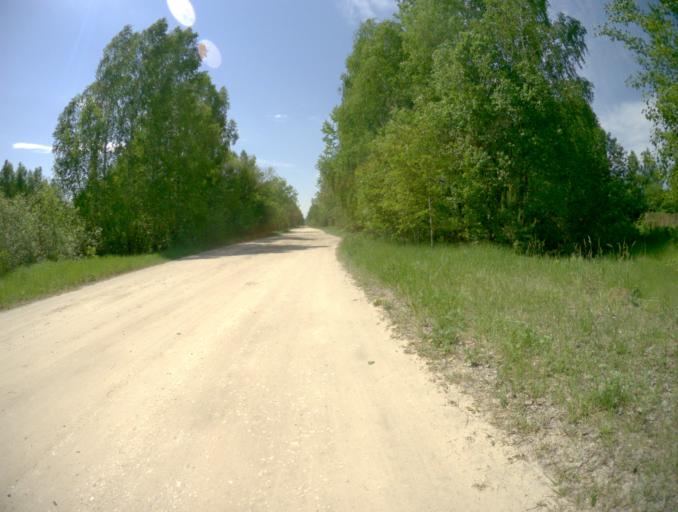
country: RU
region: Vladimir
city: Gusevskiy
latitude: 55.6755
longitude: 40.4893
